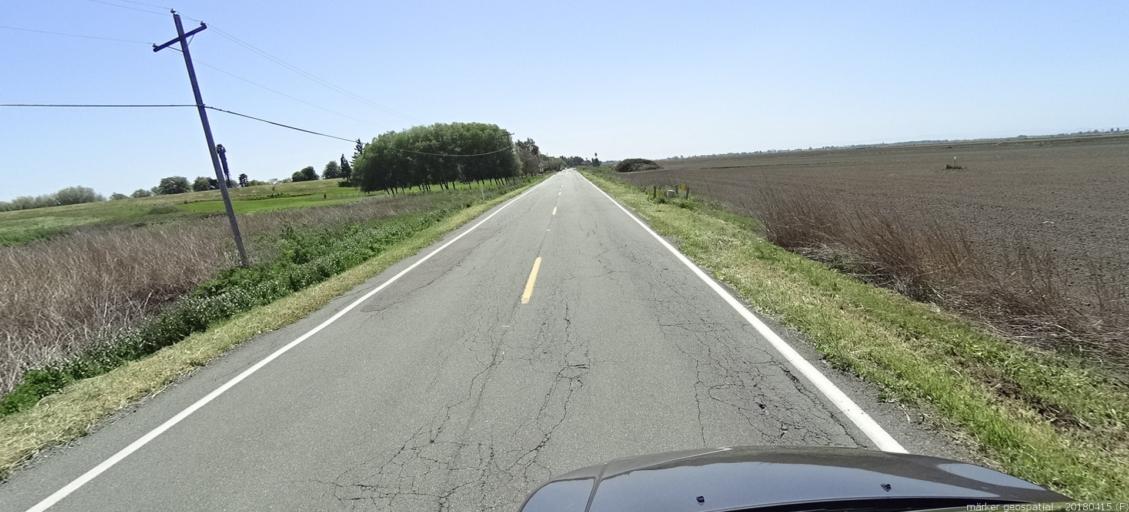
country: US
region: California
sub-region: Solano County
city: Rio Vista
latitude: 38.1461
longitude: -121.6038
